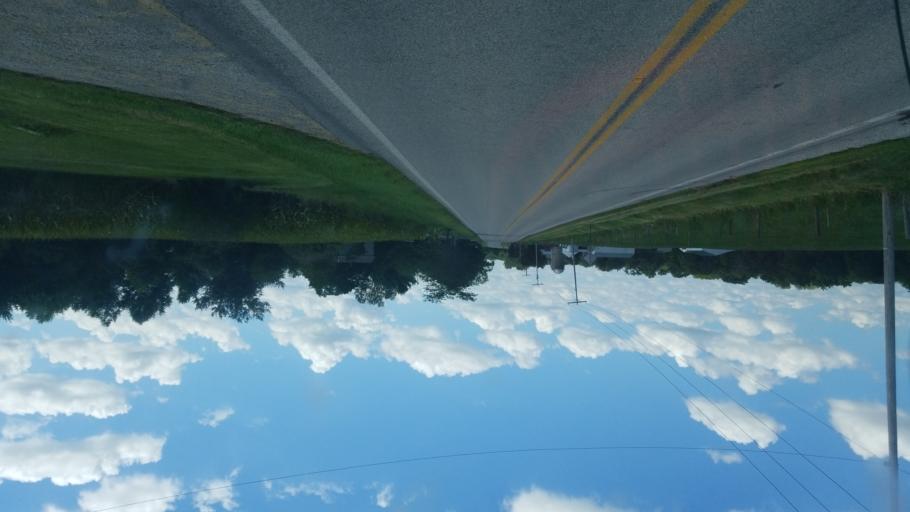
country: US
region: Ohio
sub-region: Marion County
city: Prospect
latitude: 40.3284
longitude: -83.1970
